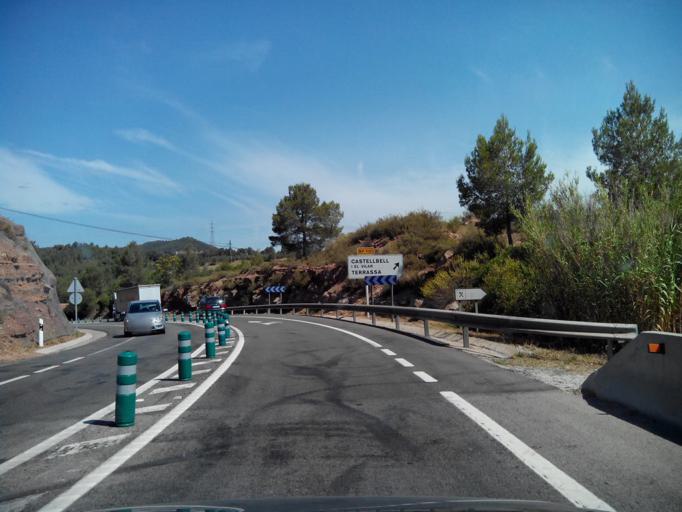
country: ES
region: Catalonia
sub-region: Provincia de Barcelona
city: Monistrol de Montserrat
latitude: 41.6196
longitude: 1.8667
